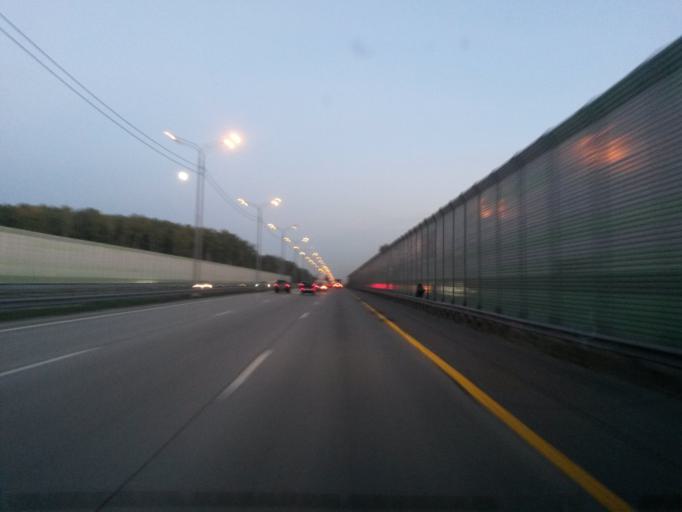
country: RU
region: Moskovskaya
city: Belyye Stolby
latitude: 55.3063
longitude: 37.8290
